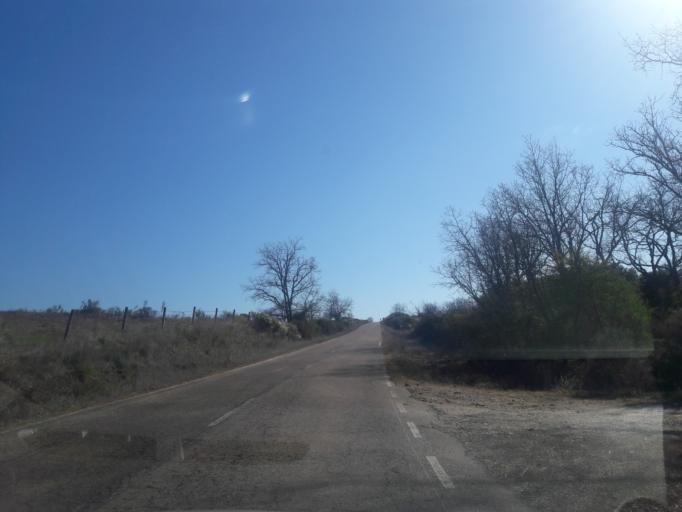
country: ES
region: Castille and Leon
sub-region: Provincia de Salamanca
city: Cabeza del Caballo
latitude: 41.1671
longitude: -6.5370
